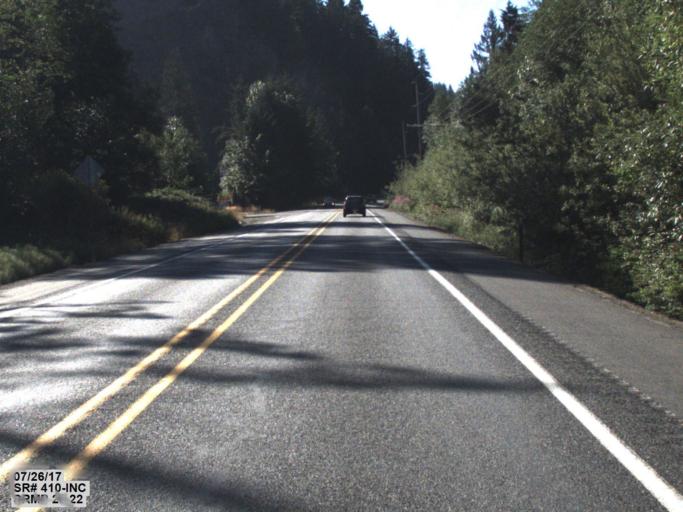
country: US
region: Washington
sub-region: King County
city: Enumclaw
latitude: 47.1802
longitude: -121.9211
